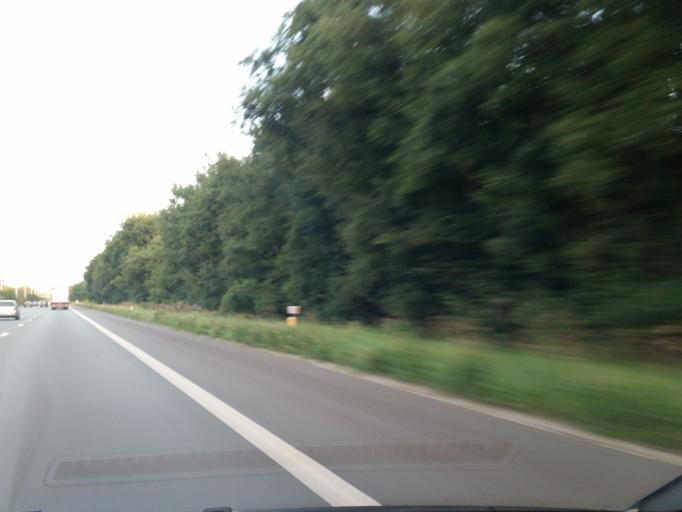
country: BE
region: Flanders
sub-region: Provincie West-Vlaanderen
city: Beernem
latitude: 51.1164
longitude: 3.3406
